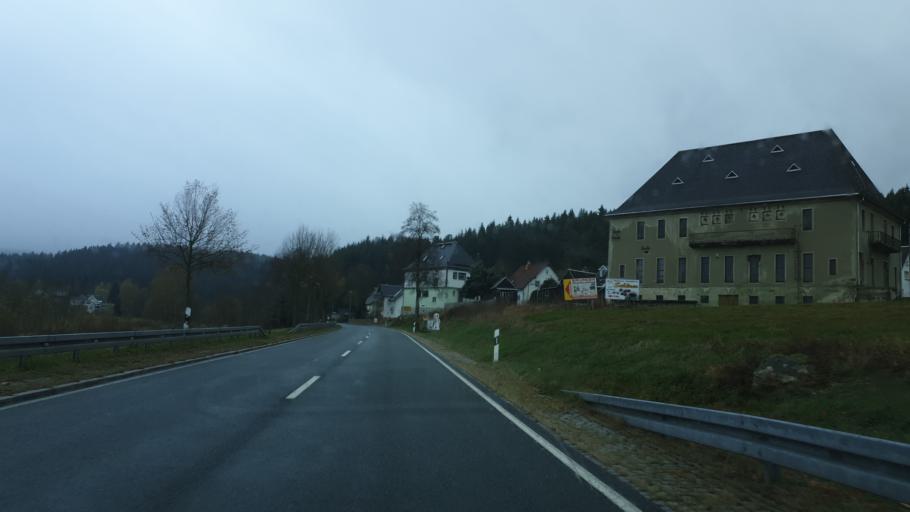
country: DE
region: Saxony
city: Muldenhammer
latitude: 50.4641
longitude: 12.4916
